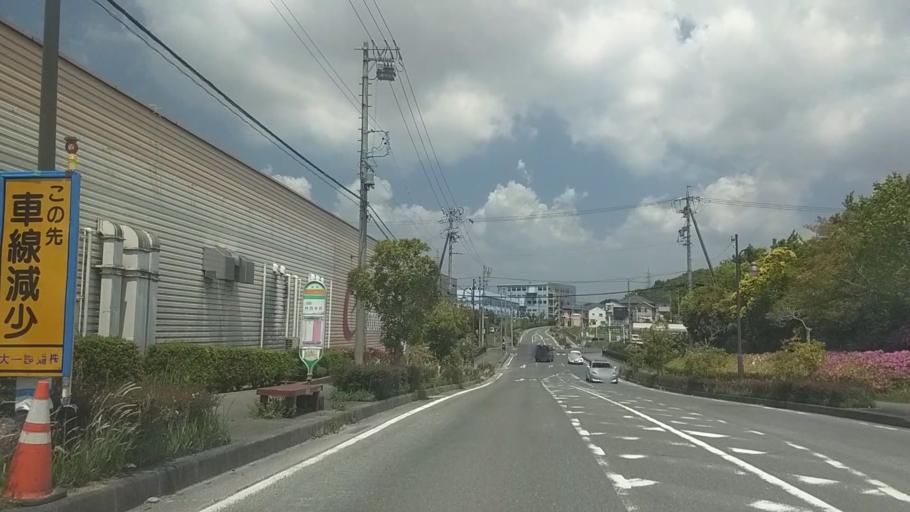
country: JP
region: Shizuoka
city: Hamamatsu
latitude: 34.7708
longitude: 137.6712
